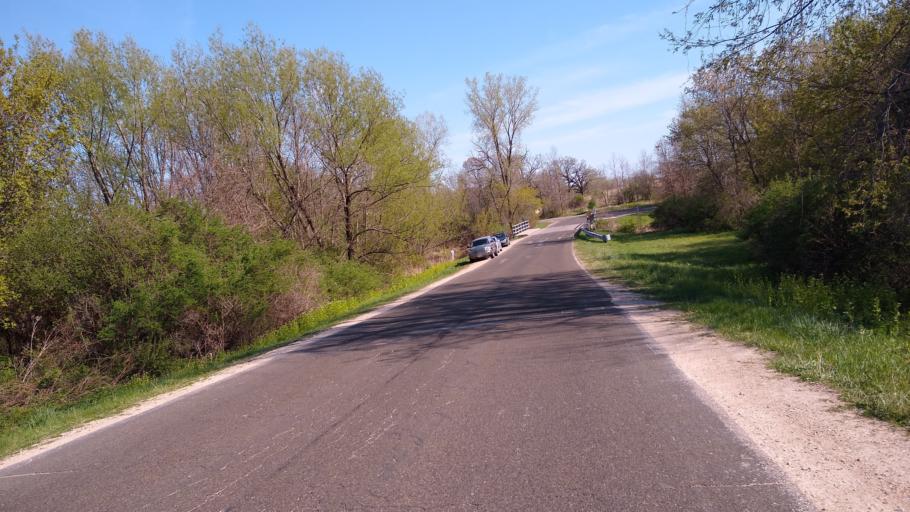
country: US
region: Wisconsin
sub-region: Dane County
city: Waunakee
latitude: 43.1418
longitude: -89.4384
